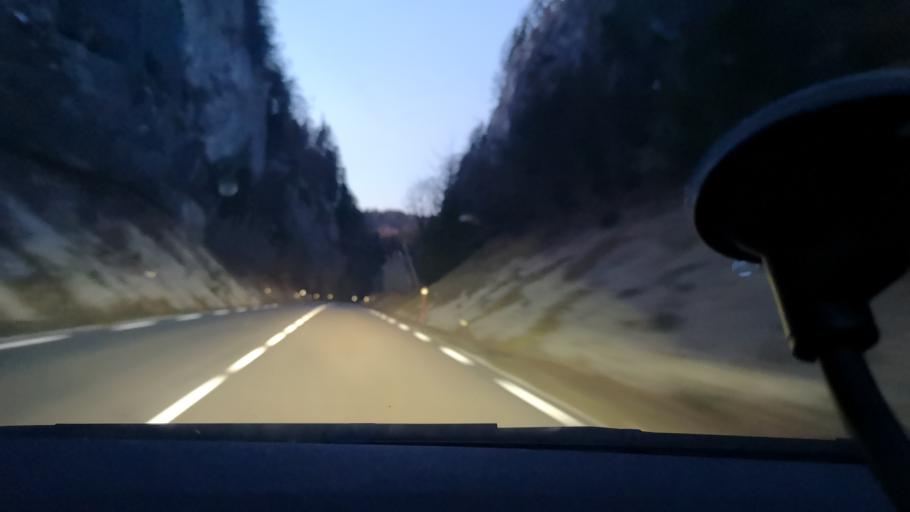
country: FR
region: Franche-Comte
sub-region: Departement du Jura
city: Champagnole
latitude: 46.7535
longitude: 5.9690
